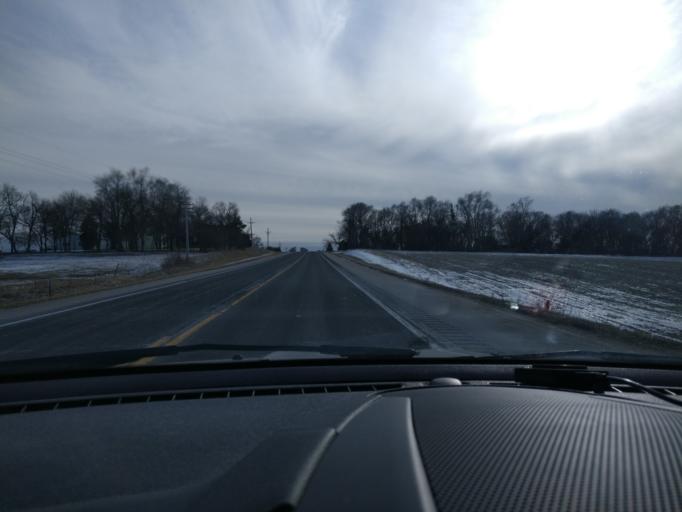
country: US
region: Nebraska
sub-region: Dodge County
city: Fremont
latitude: 41.3504
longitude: -96.5022
